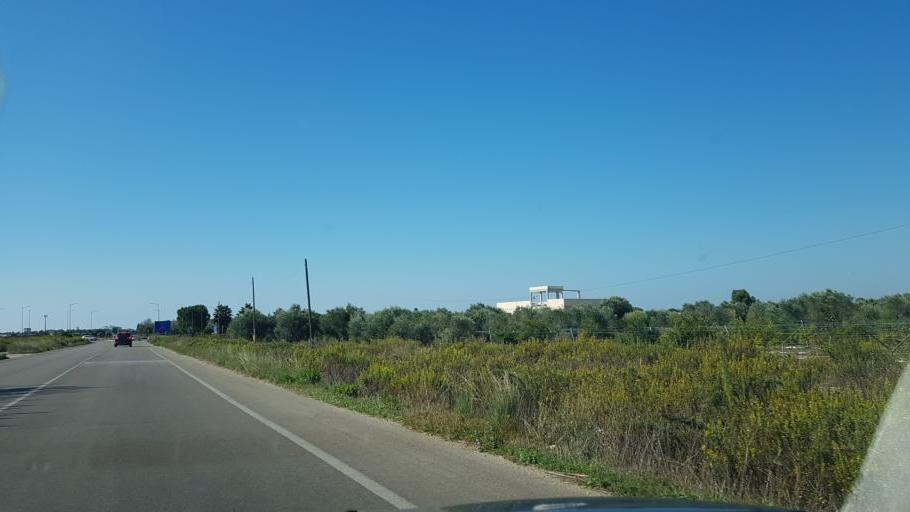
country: IT
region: Apulia
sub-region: Provincia di Lecce
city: Leverano
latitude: 40.3033
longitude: 18.0123
